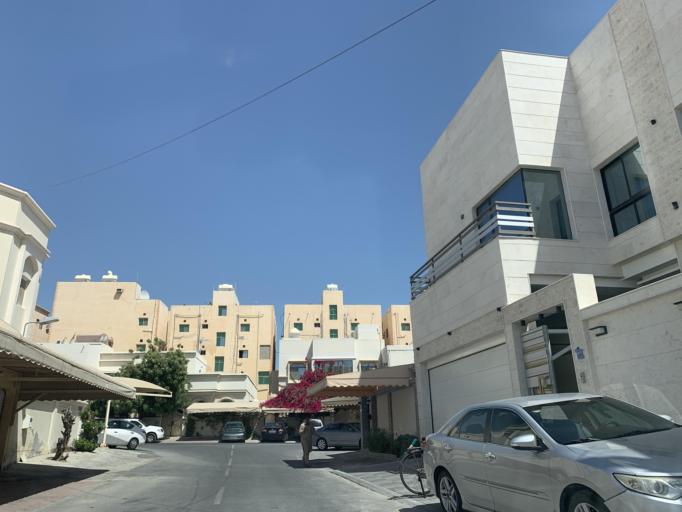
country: BH
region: Northern
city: Ar Rifa'
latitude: 26.1380
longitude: 50.5776
